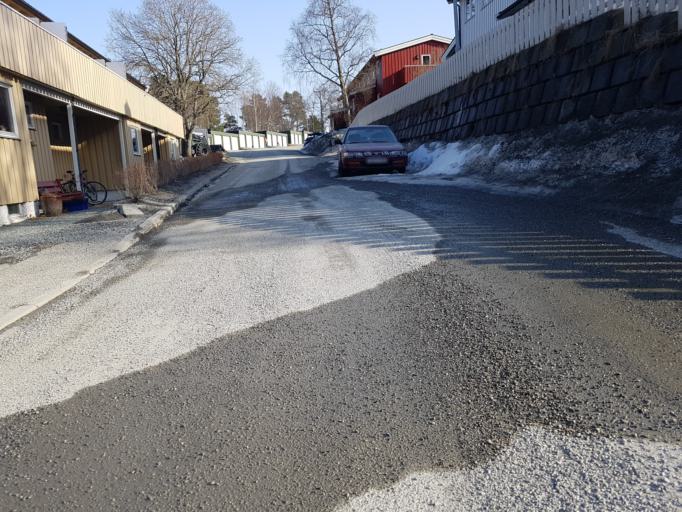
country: NO
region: Sor-Trondelag
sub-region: Trondheim
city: Trondheim
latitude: 63.4299
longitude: 10.3468
